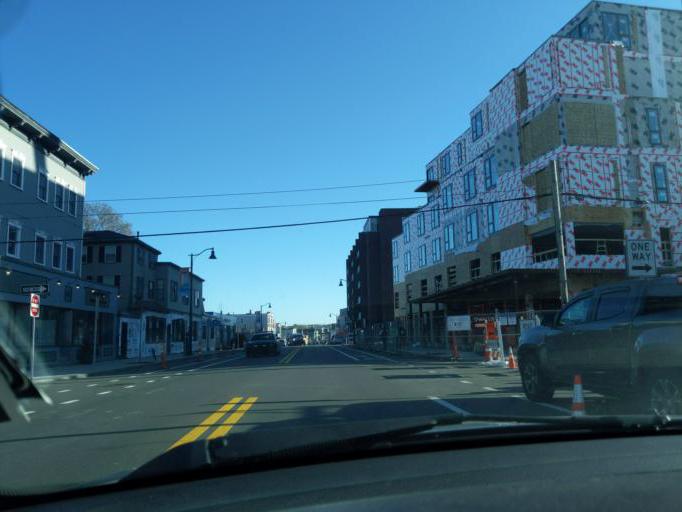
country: US
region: Massachusetts
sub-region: Essex County
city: Beverly
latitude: 42.5481
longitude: -70.8840
